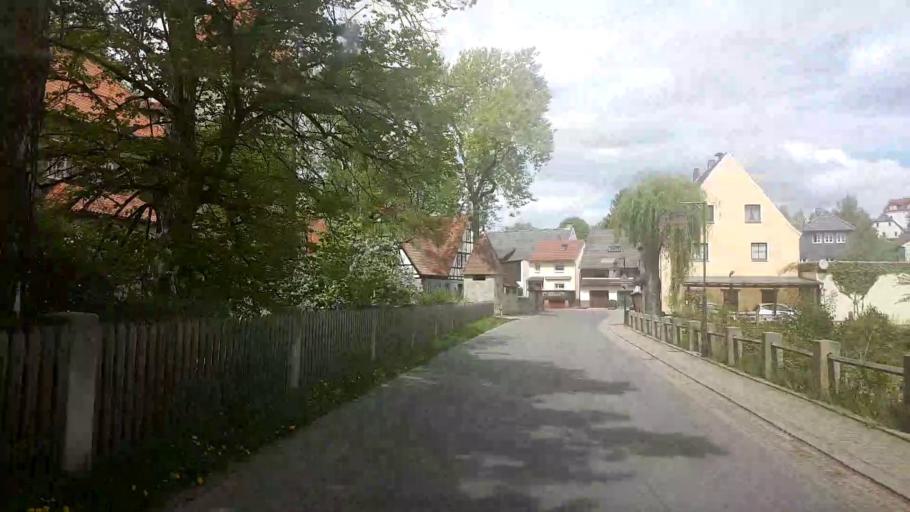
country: DE
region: Bavaria
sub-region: Upper Franconia
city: Untersiemau
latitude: 50.1921
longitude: 10.9751
